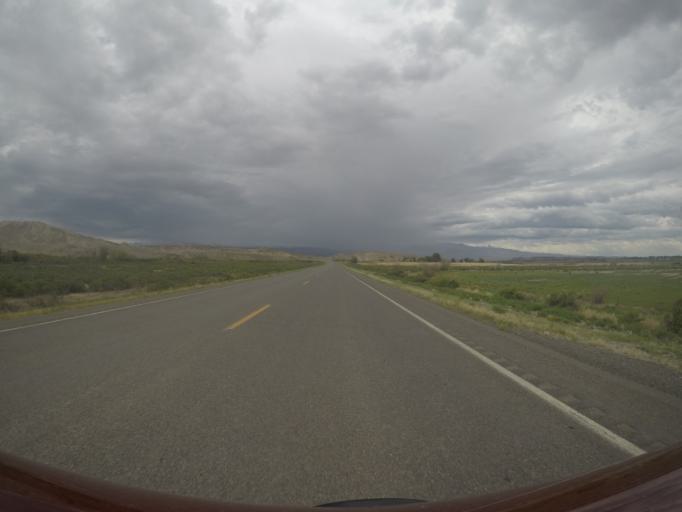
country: US
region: Wyoming
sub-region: Big Horn County
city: Lovell
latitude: 44.8774
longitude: -108.2991
